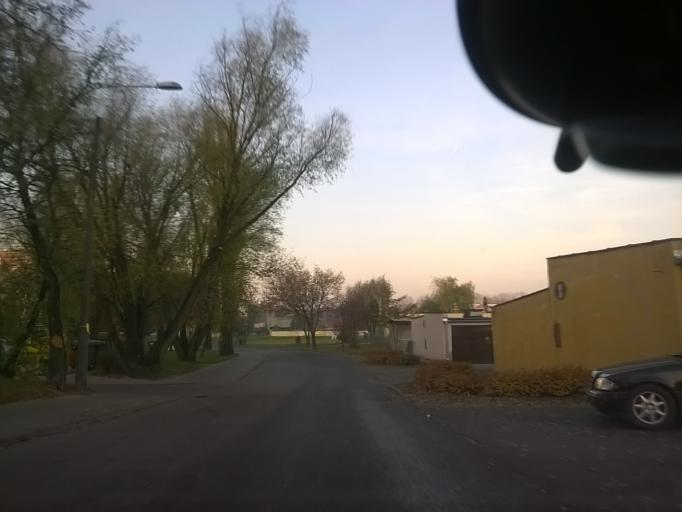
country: PL
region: Warmian-Masurian Voivodeship
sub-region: Powiat ketrzynski
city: Ketrzyn
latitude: 54.0837
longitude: 21.3689
